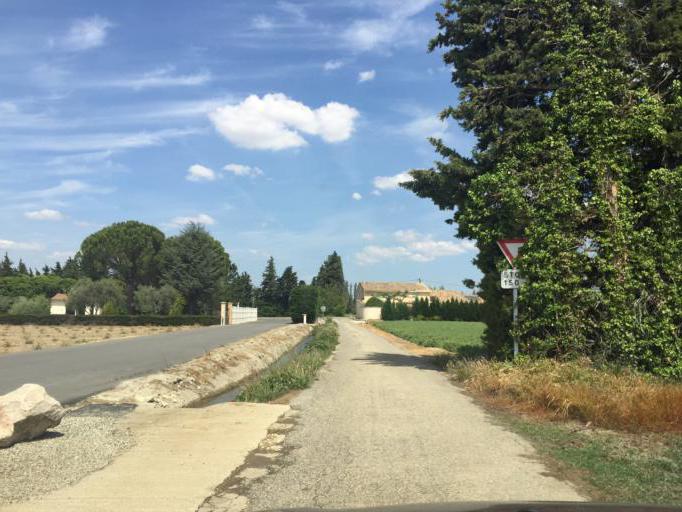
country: FR
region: Provence-Alpes-Cote d'Azur
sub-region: Departement du Vaucluse
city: Jonquieres
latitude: 44.1232
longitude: 4.9223
